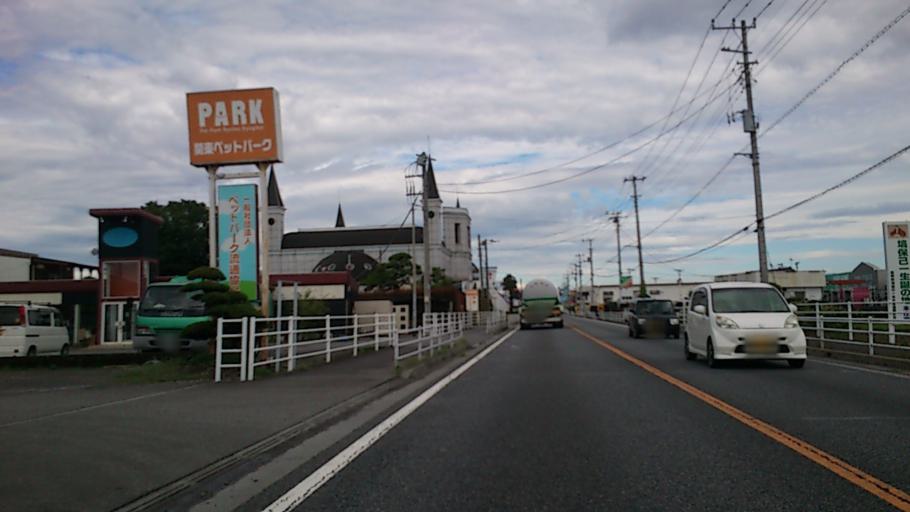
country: JP
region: Saitama
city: Honjo
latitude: 36.2550
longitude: 139.1612
